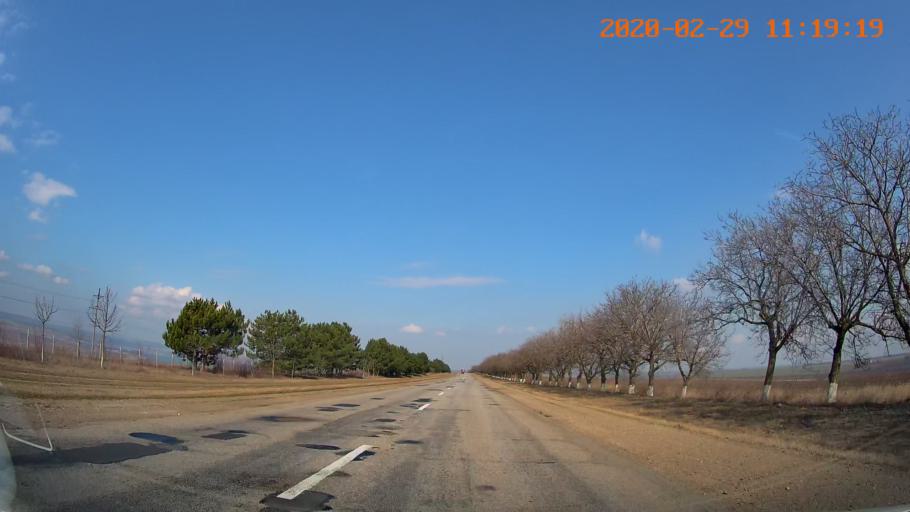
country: MD
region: Telenesti
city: Cocieri
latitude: 47.3479
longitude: 29.1751
